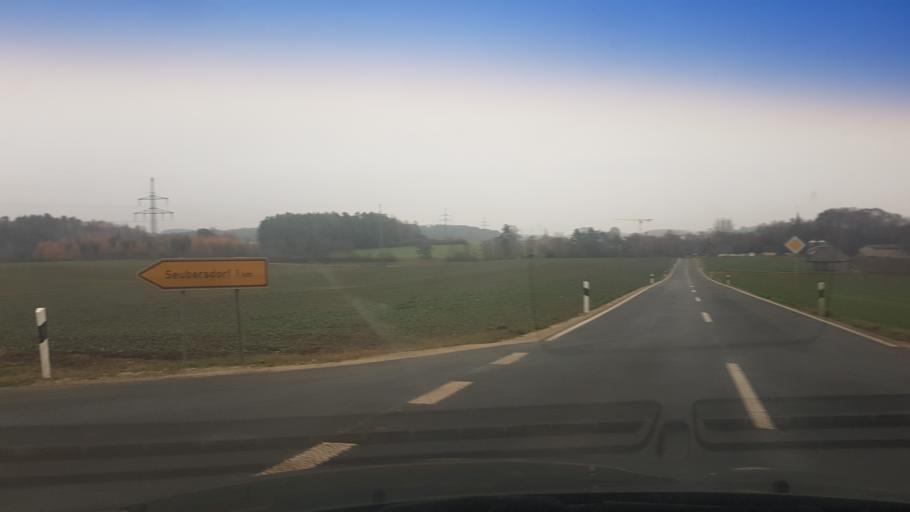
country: DE
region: Bavaria
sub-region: Upper Franconia
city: Wonsees
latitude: 50.0277
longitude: 11.2939
